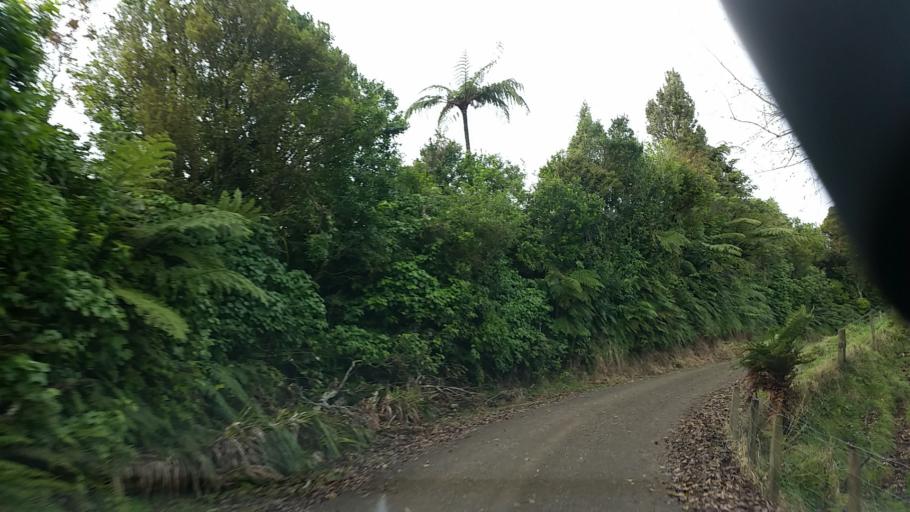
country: NZ
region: Taranaki
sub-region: New Plymouth District
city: Waitara
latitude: -39.0687
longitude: 174.3993
